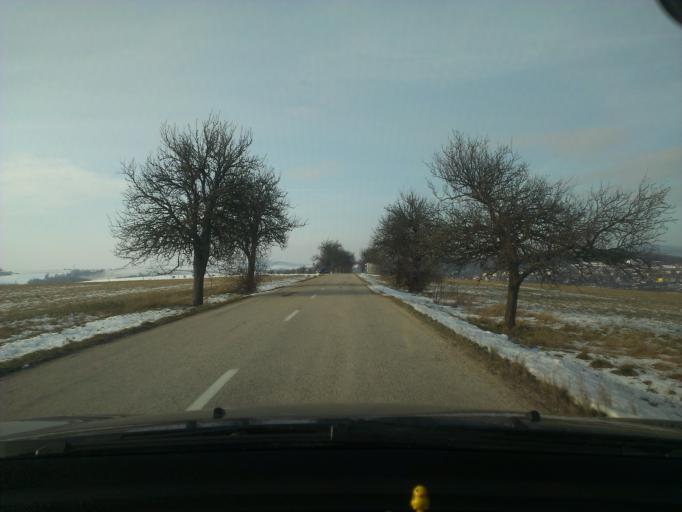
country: SK
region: Nitriansky
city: Stara Tura
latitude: 48.7467
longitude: 17.6410
